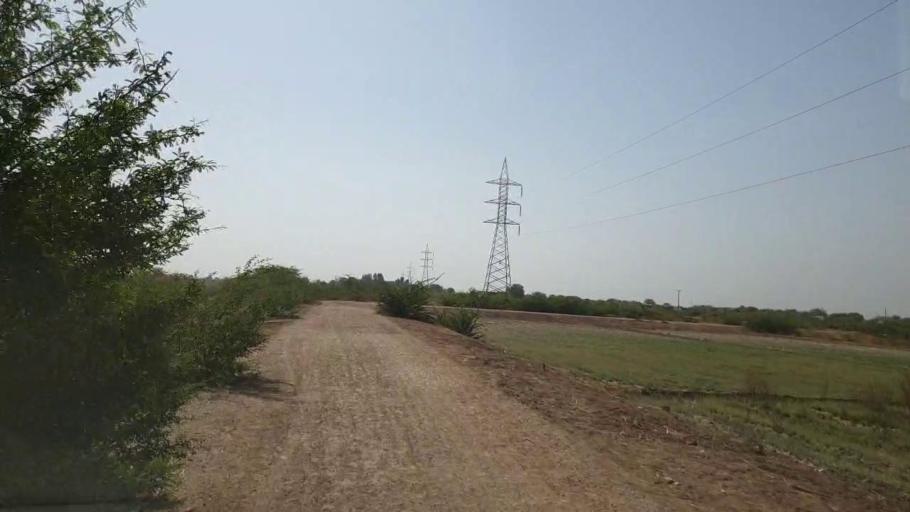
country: PK
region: Sindh
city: Naukot
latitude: 24.9911
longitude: 69.4753
